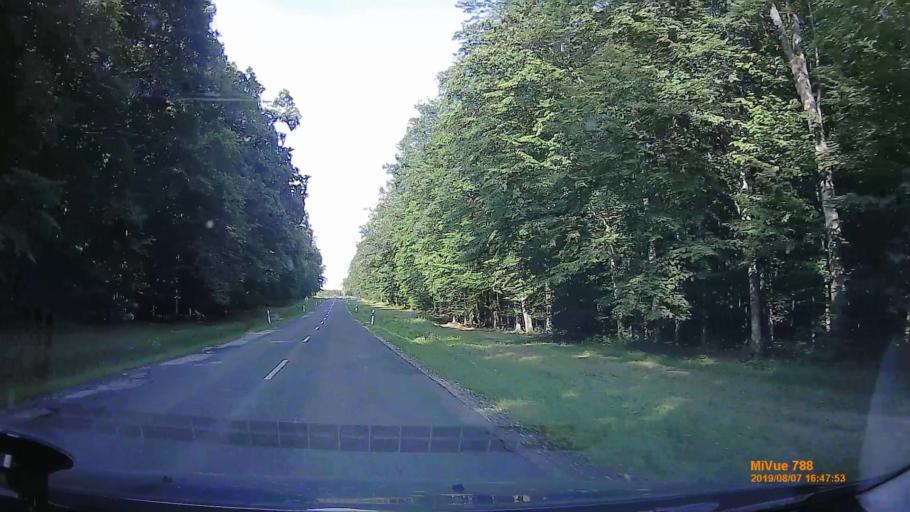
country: HU
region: Zala
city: Lenti
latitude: 46.6673
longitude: 16.6403
